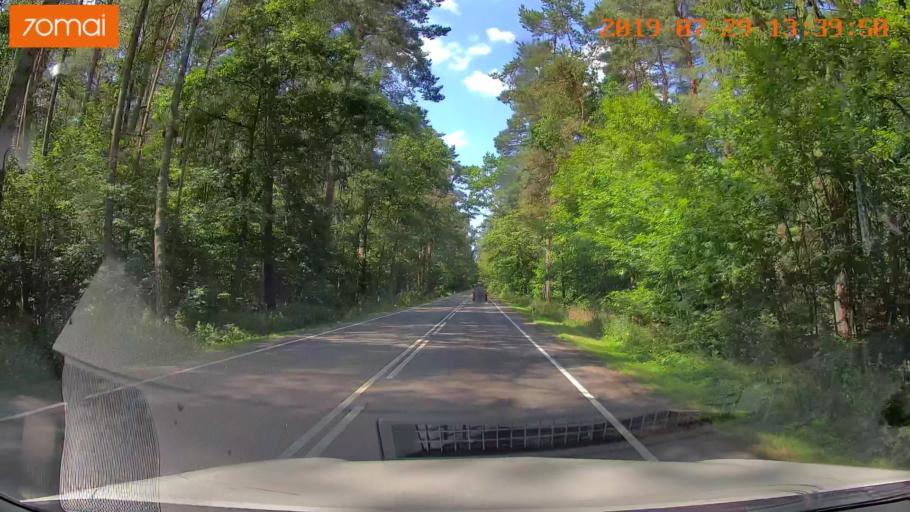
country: RU
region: Kaliningrad
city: Svetlyy
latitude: 54.7251
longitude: 20.1464
